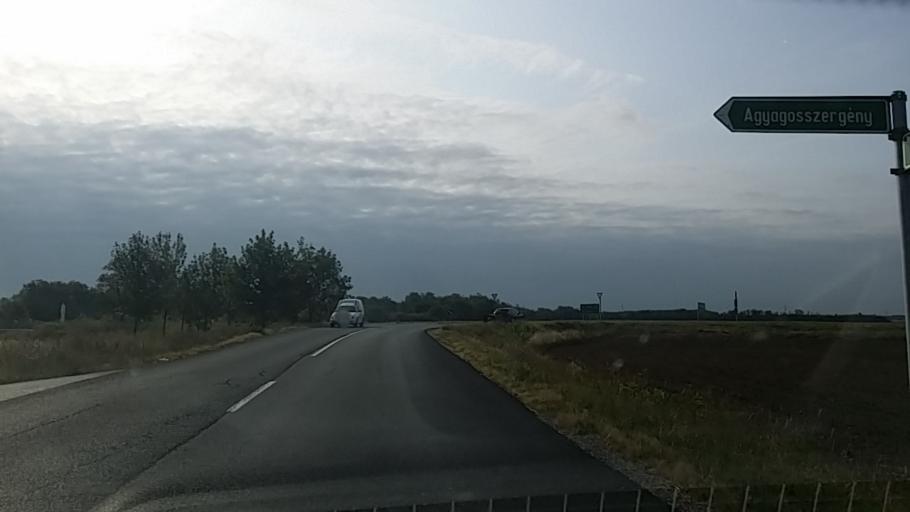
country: HU
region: Gyor-Moson-Sopron
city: Fertoszentmiklos
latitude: 47.5980
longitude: 16.9159
